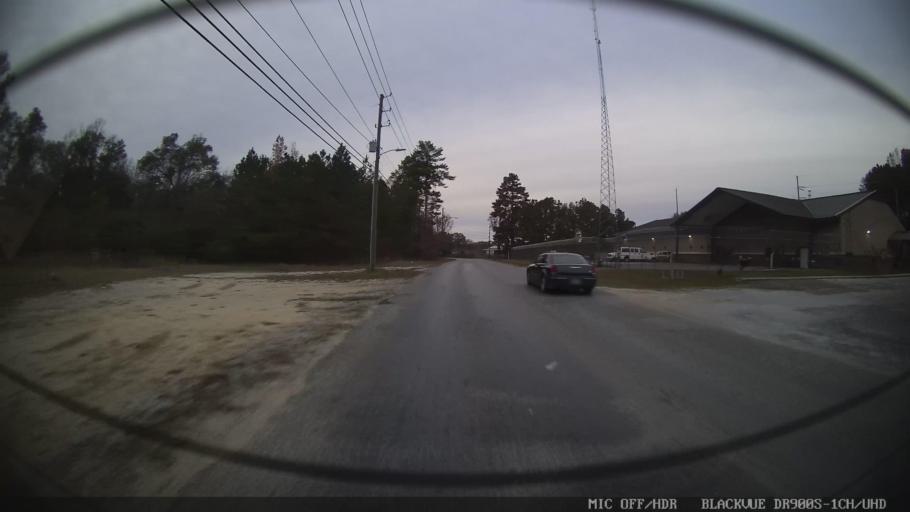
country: US
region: Mississippi
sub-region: Clarke County
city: Quitman
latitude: 32.0408
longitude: -88.7347
